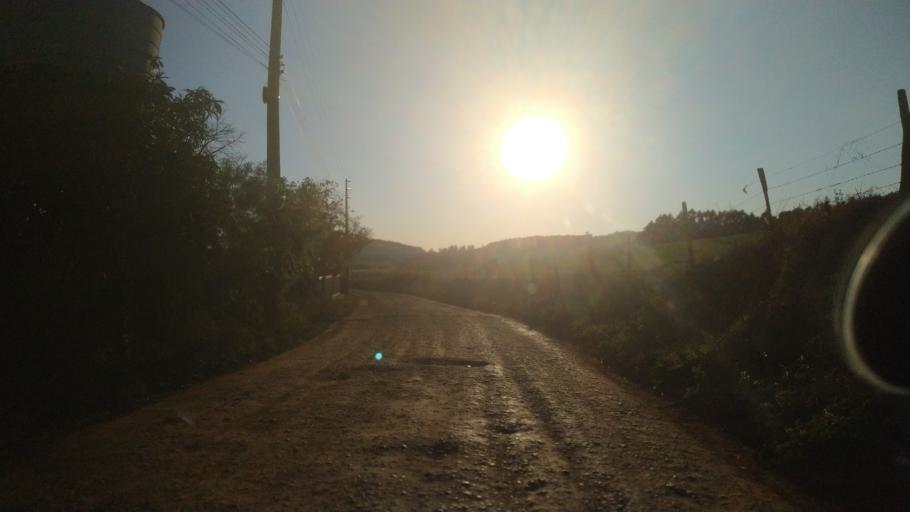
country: BR
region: Santa Catarina
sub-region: Chapeco
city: Chapeco
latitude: -27.0385
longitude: -52.6321
